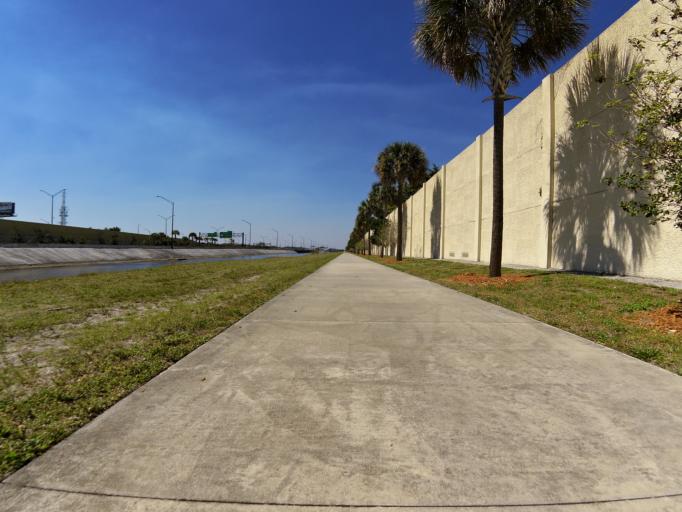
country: US
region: Florida
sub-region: Broward County
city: Pine Island Ridge
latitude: 26.1083
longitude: -80.2838
